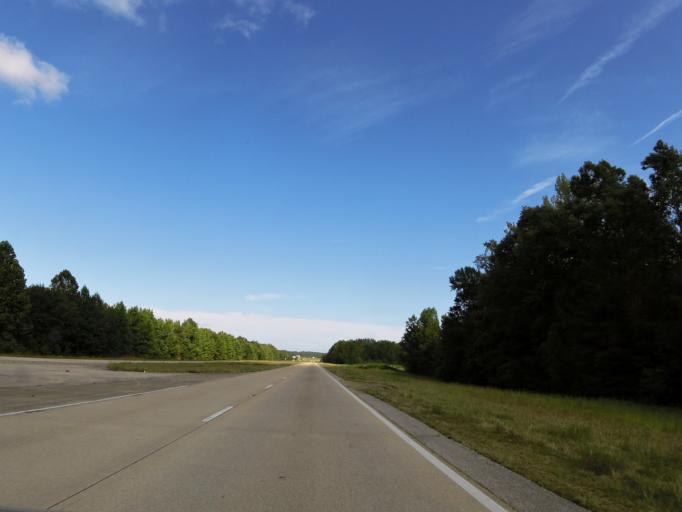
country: US
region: Mississippi
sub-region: Tishomingo County
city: Iuka
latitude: 34.8052
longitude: -88.2507
